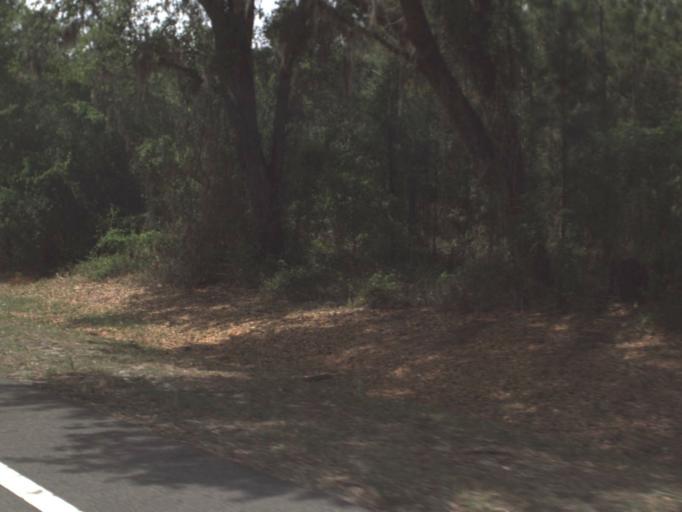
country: US
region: Florida
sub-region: Putnam County
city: Crescent City
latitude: 29.5020
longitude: -81.4873
